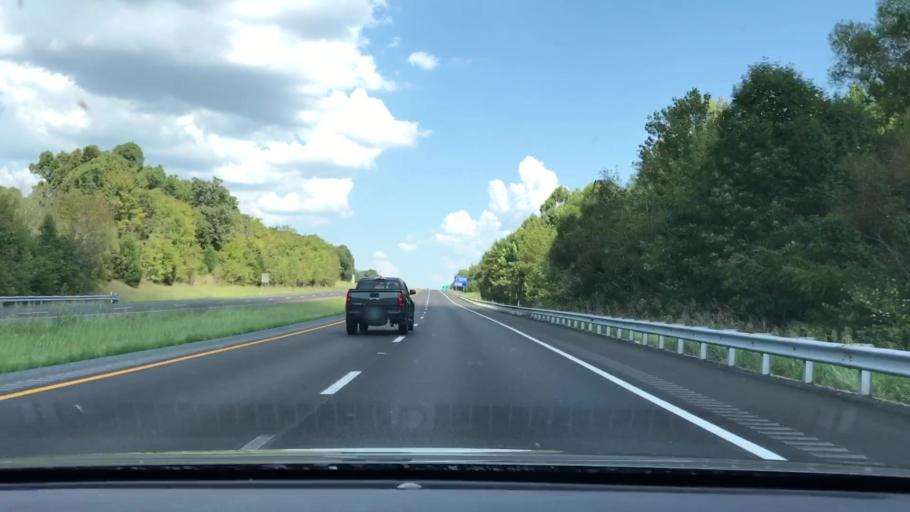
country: US
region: Kentucky
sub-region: Lyon County
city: Eddyville
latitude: 37.0978
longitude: -88.0409
